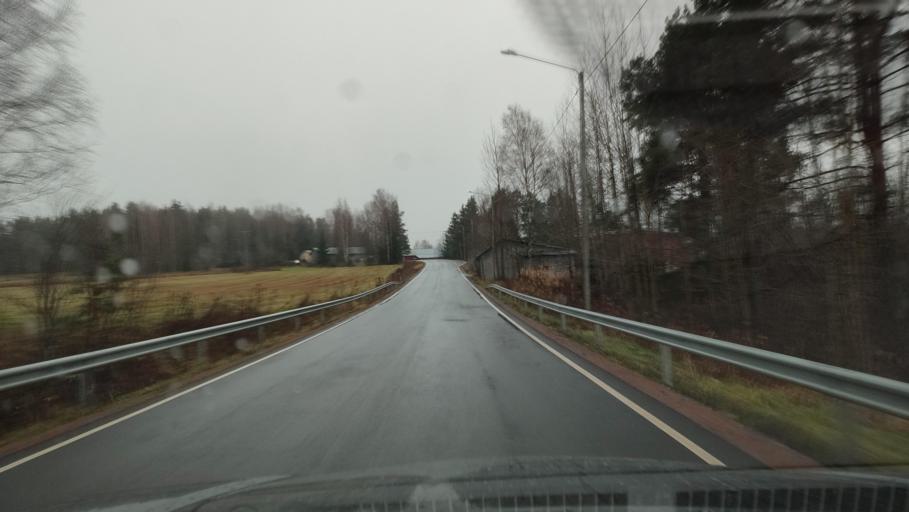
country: FI
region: Southern Ostrobothnia
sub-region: Suupohja
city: Karijoki
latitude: 62.1438
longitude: 21.6877
